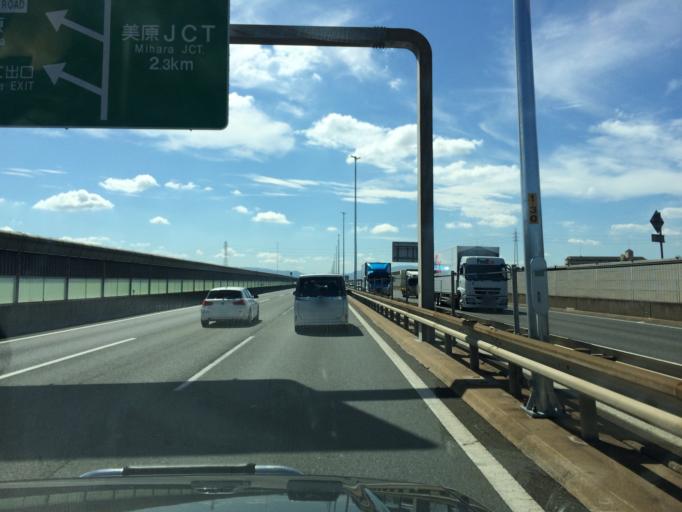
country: JP
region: Osaka
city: Matsubara
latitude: 34.5735
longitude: 135.5637
